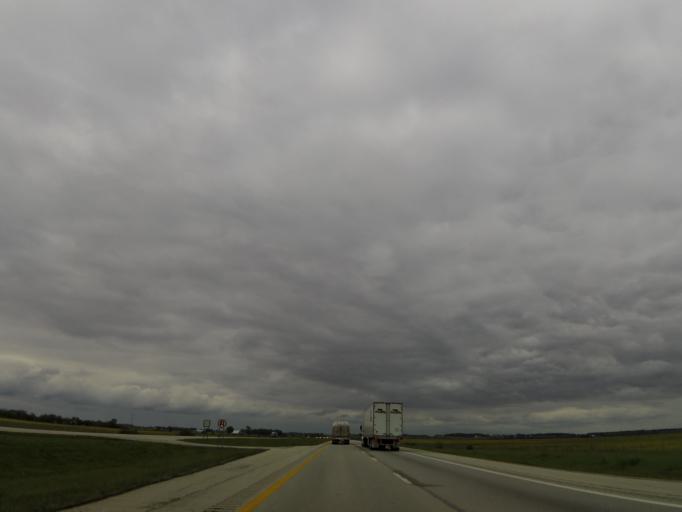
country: US
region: Ohio
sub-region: Greene County
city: Shawnee Hills
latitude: 39.5415
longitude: -83.7666
